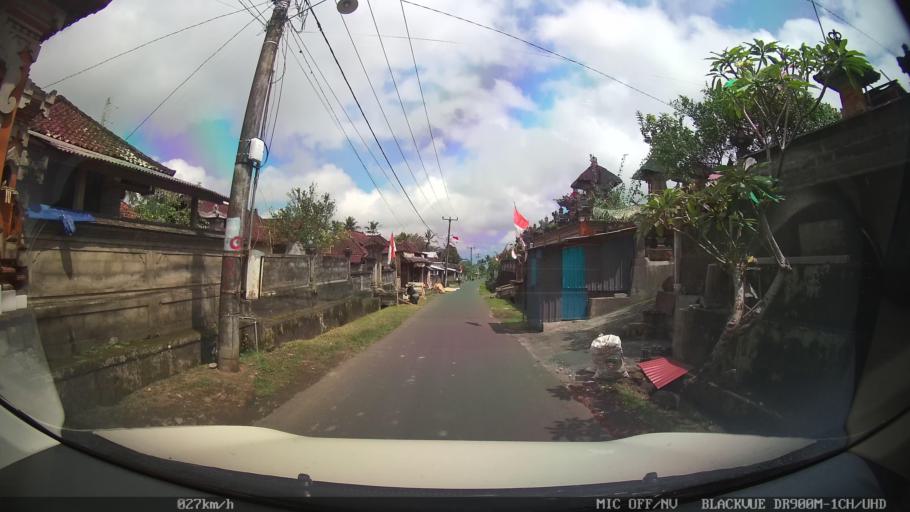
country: ID
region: Bali
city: Banjar Susut Kaja
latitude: -8.4425
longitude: 115.3298
